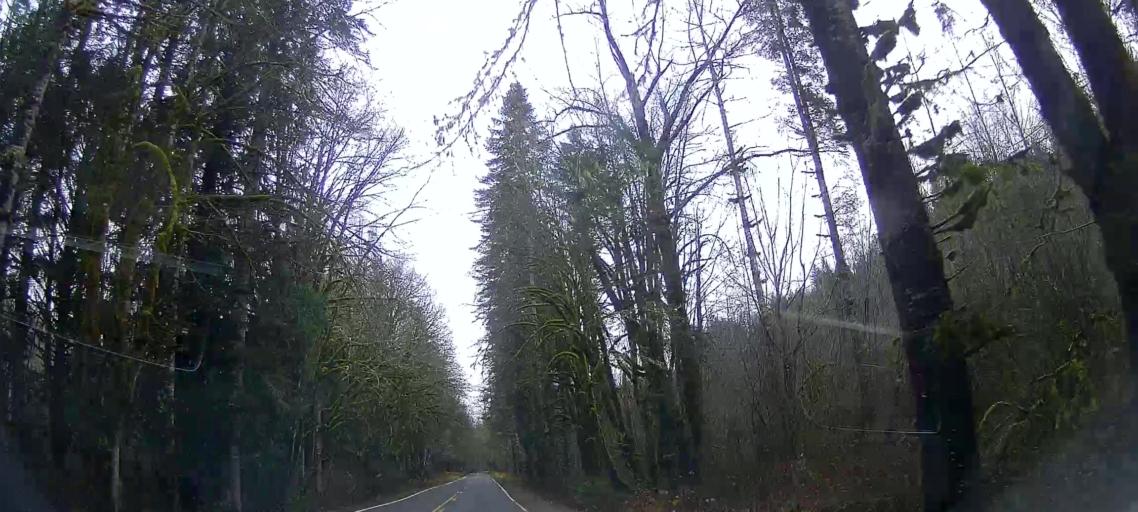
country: US
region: Washington
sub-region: Skagit County
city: Sedro-Woolley
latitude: 48.5101
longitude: -121.8870
